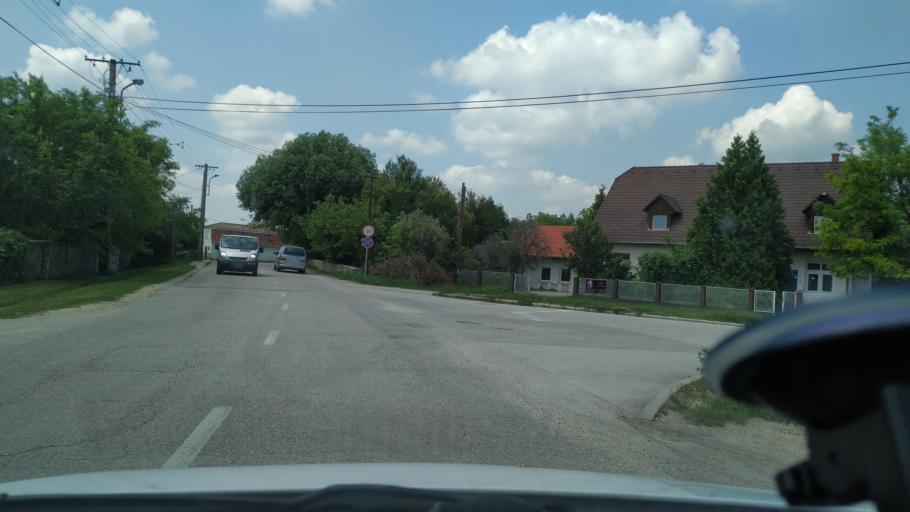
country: HU
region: Veszprem
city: Varpalota
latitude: 47.2004
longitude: 18.1789
